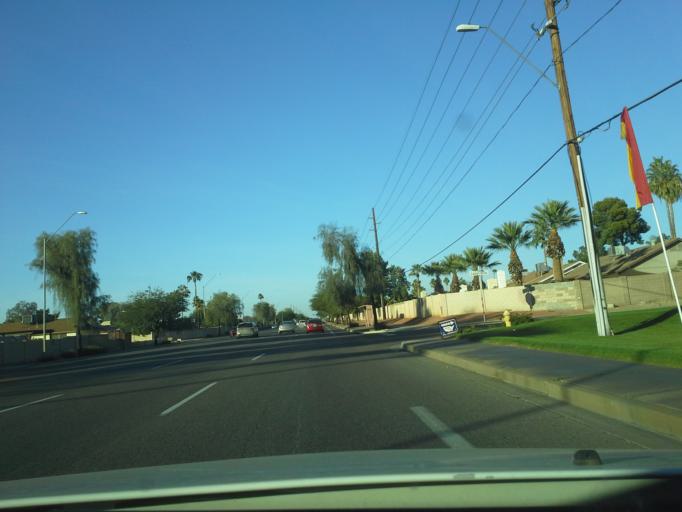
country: US
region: Arizona
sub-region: Maricopa County
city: Glendale
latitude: 33.6427
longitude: -112.1344
